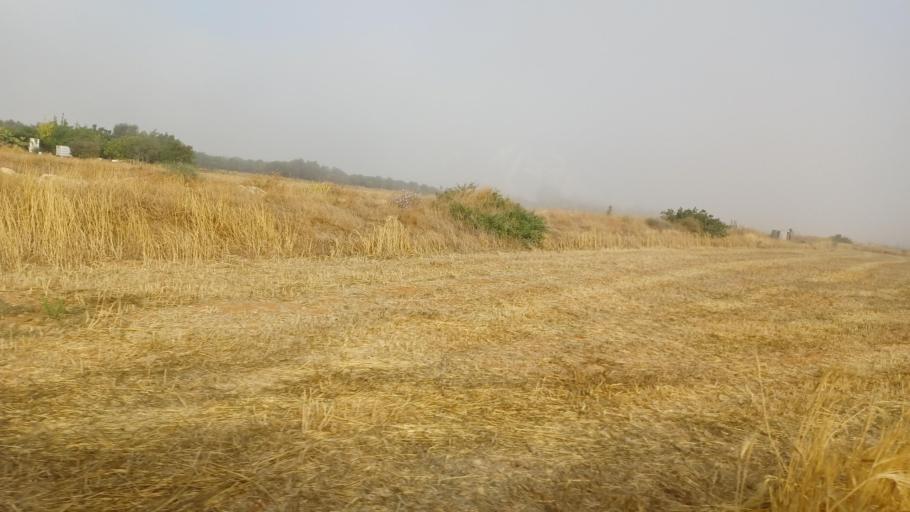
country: CY
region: Ammochostos
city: Acheritou
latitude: 35.1029
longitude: 33.8798
